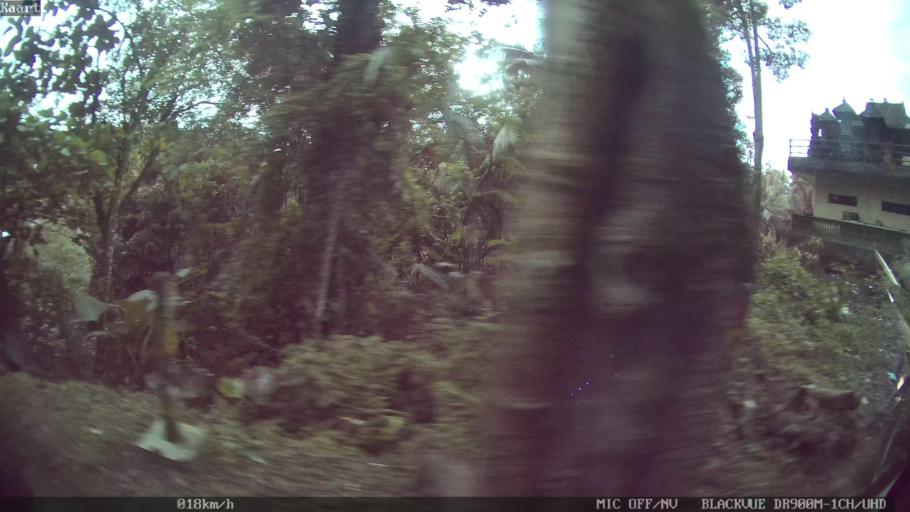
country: ID
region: Bali
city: Banjar Kubu
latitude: -8.4074
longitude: 115.4243
